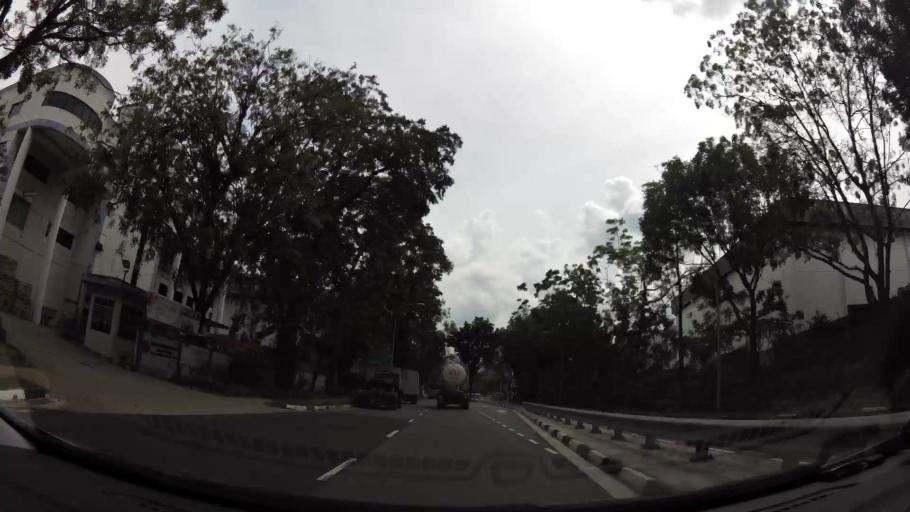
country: MY
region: Johor
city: Johor Bahru
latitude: 1.4093
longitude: 103.7463
